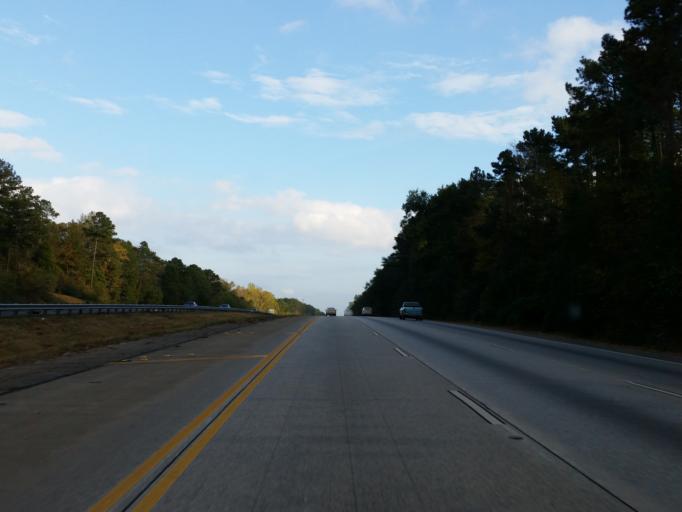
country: US
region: Georgia
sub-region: Monroe County
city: Forsyth
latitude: 33.0205
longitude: -83.8957
